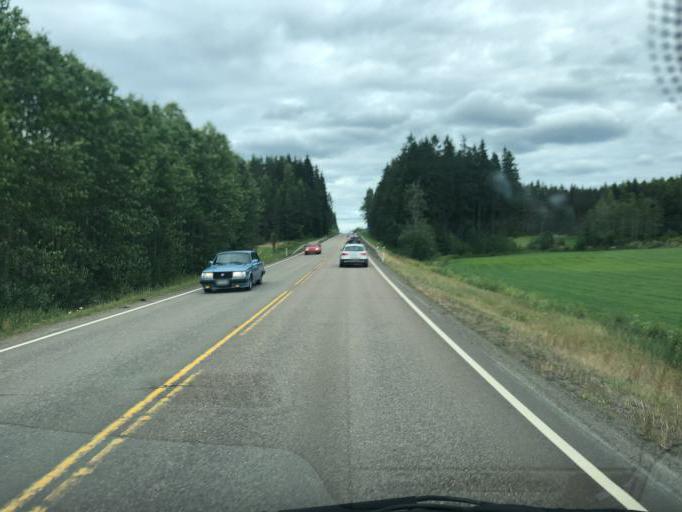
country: FI
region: Southern Savonia
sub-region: Mikkeli
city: Maentyharju
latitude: 61.0635
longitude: 27.0521
